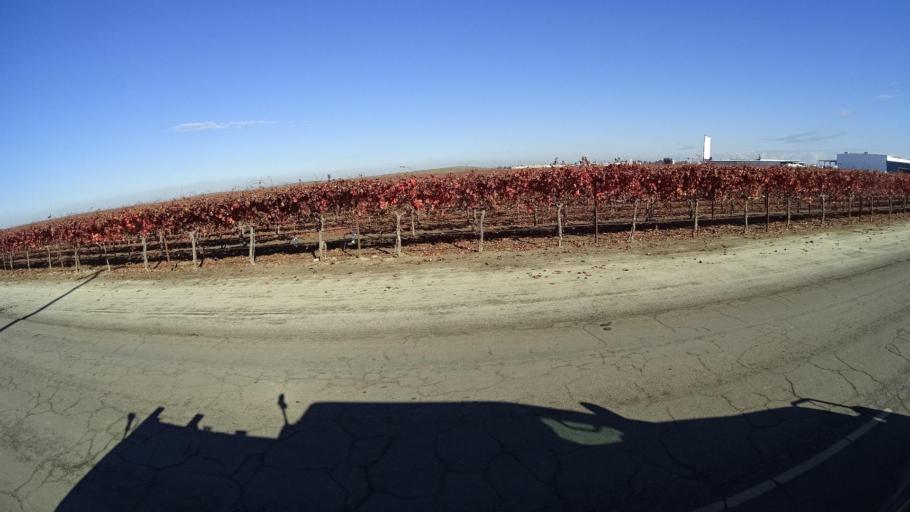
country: US
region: California
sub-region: Kern County
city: Delano
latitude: 35.7323
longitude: -119.2510
